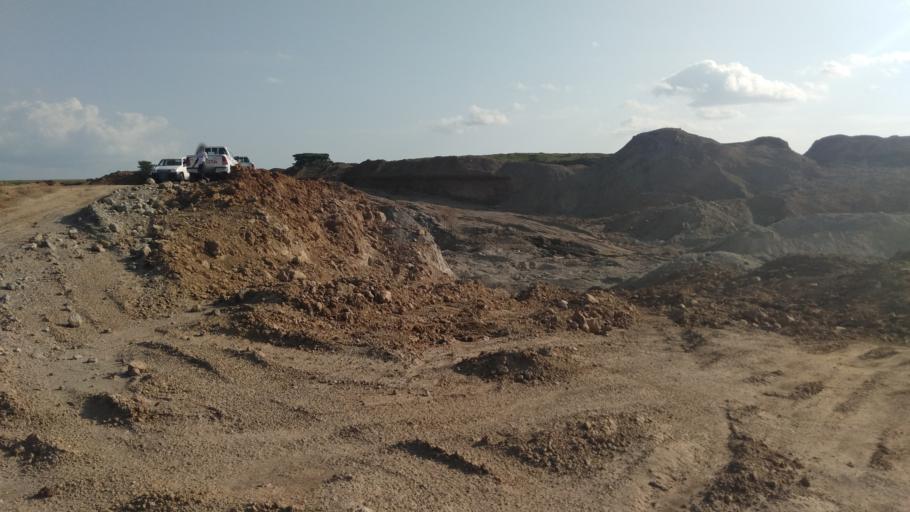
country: ET
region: Oromiya
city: Shashemene
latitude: 7.3163
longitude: 38.6261
